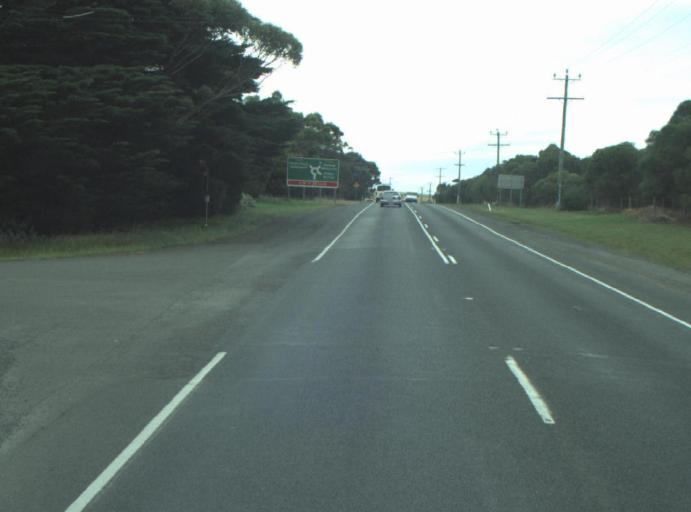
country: AU
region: Victoria
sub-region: Greater Geelong
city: Clifton Springs
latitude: -38.1816
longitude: 144.5532
